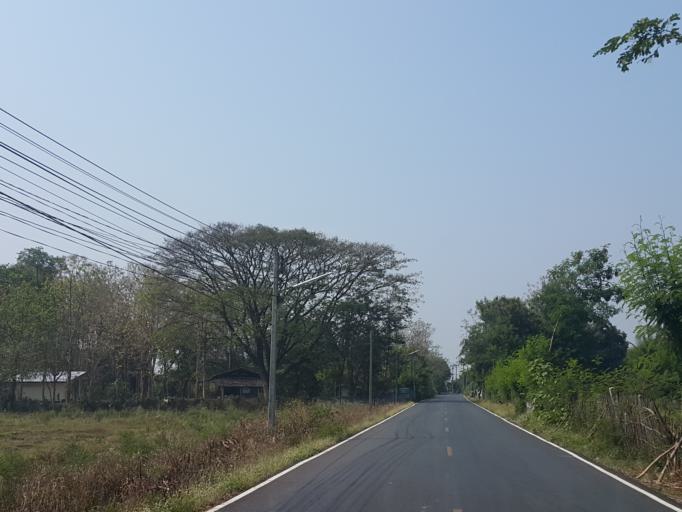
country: TH
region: Chiang Mai
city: San Kamphaeng
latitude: 18.7530
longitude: 99.1397
